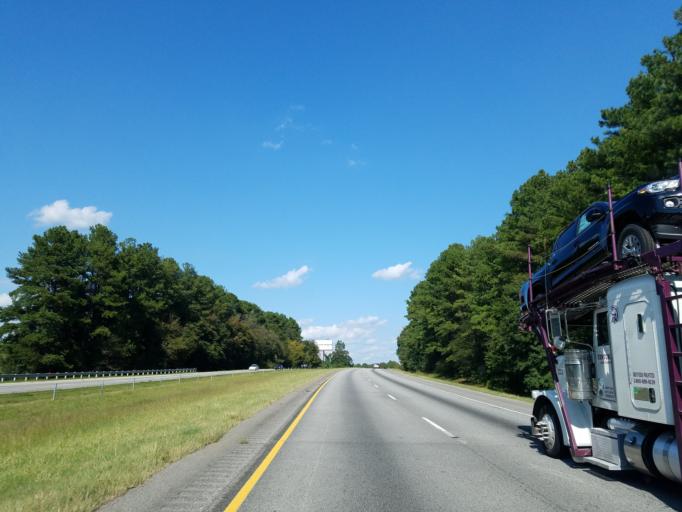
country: US
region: Georgia
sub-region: Banks County
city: Homer
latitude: 34.3239
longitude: -83.3637
